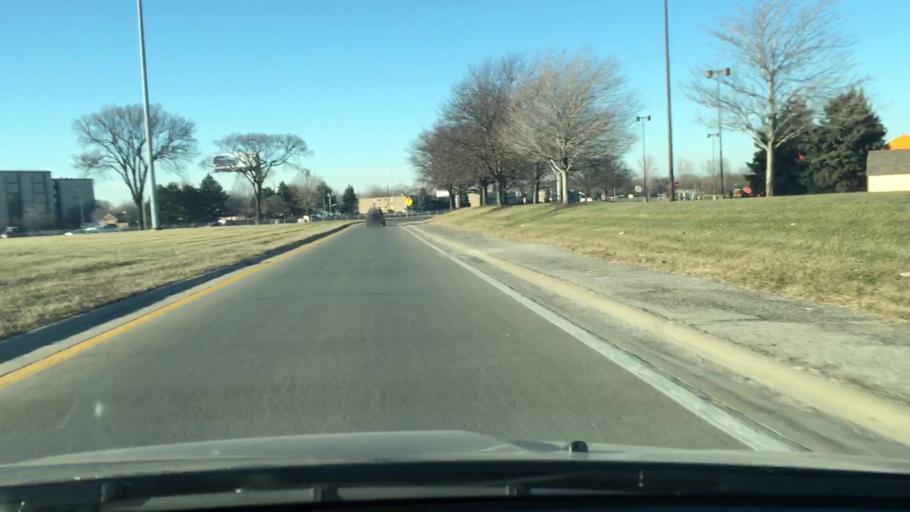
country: US
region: Michigan
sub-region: Wayne County
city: Dearborn
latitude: 42.3306
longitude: -83.2143
